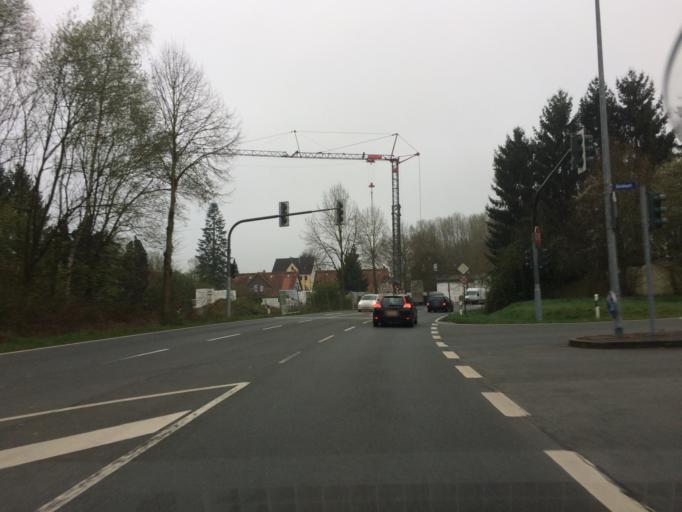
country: DE
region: North Rhine-Westphalia
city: Hattingen
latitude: 51.4292
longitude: 7.1739
